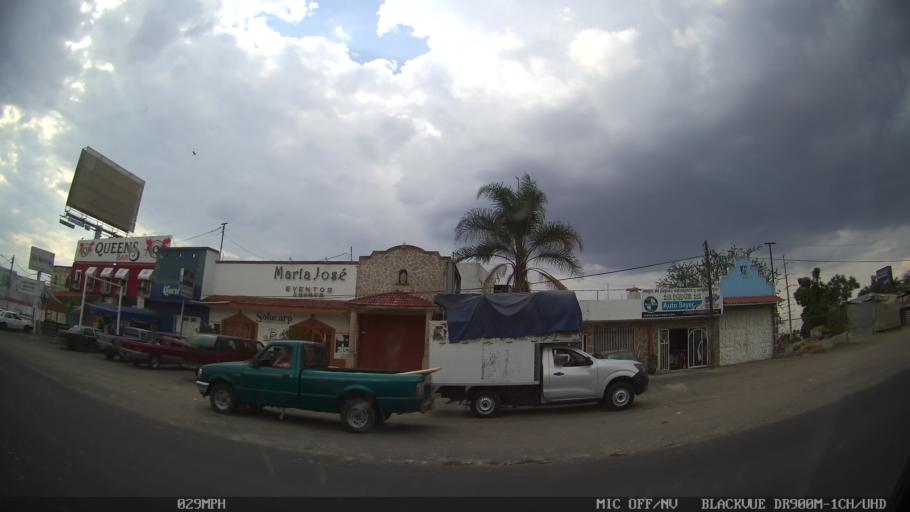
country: MX
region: Jalisco
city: Tlaquepaque
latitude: 20.6171
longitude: -103.2709
